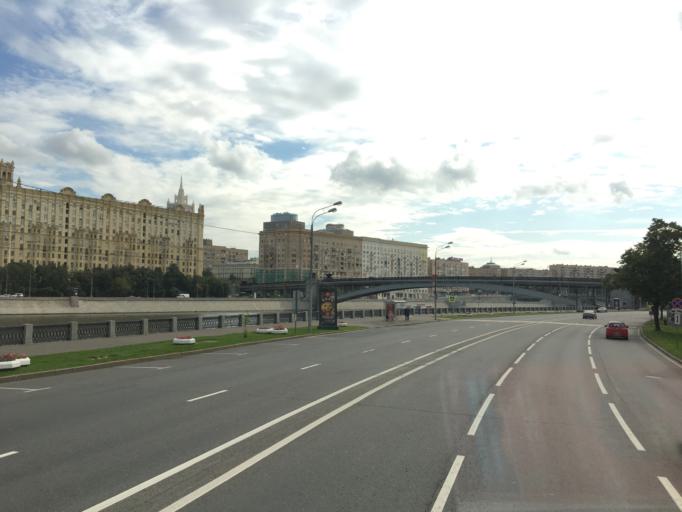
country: RU
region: Moskovskaya
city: Dorogomilovo
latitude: 55.7504
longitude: 37.5720
